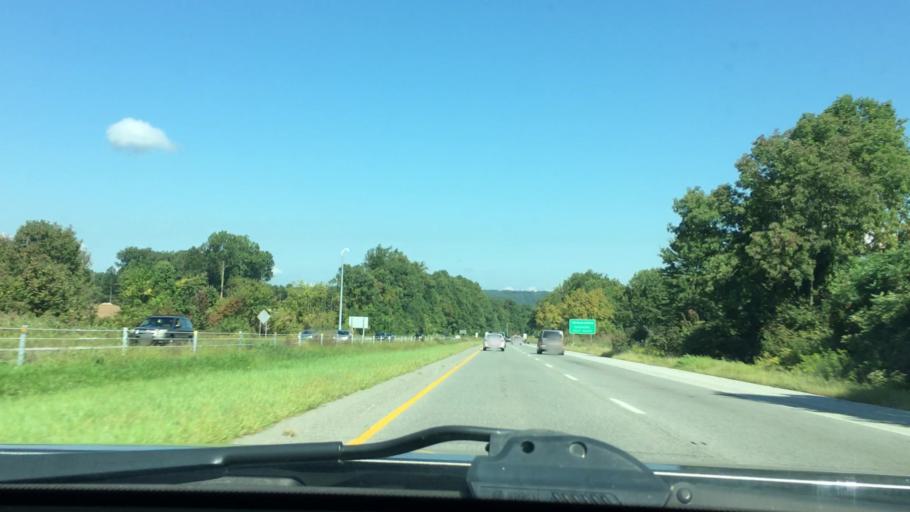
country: US
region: Pennsylvania
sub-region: Chester County
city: Exton
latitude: 40.0207
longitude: -75.5866
